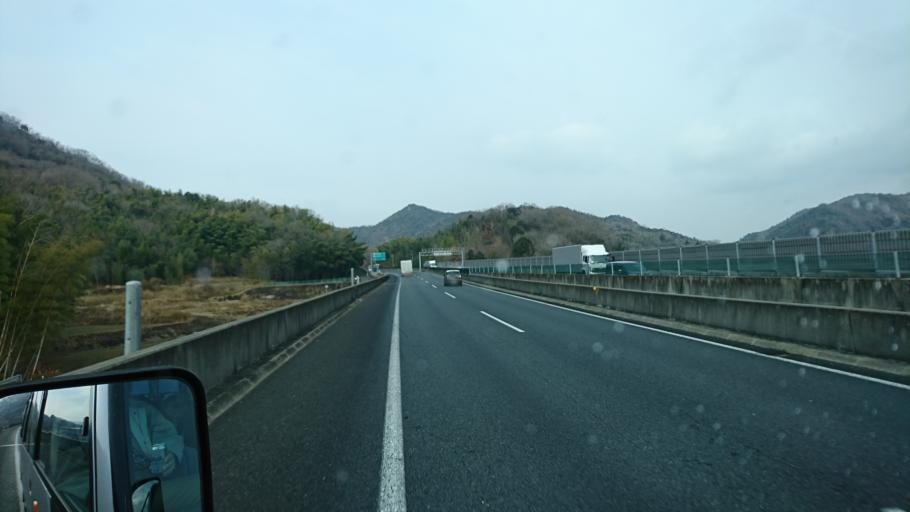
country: JP
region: Hyogo
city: Kakogawacho-honmachi
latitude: 34.8485
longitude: 134.8114
